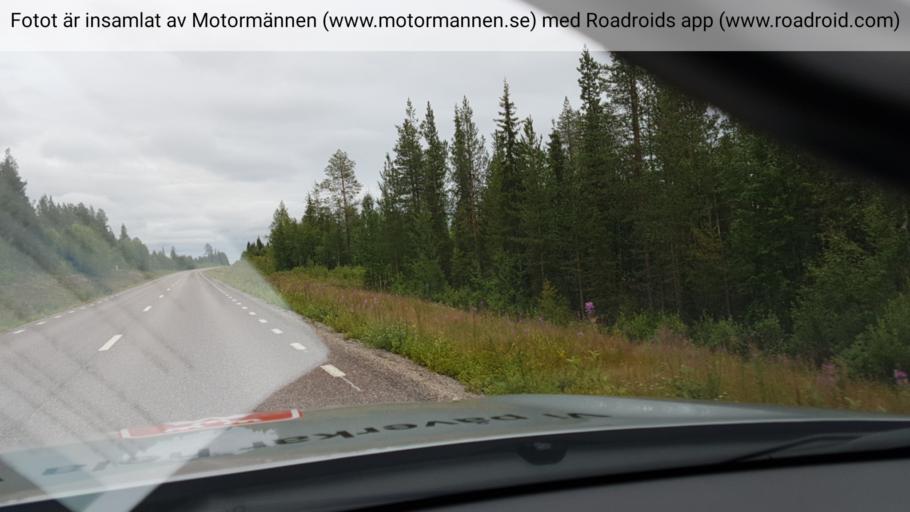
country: SE
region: Norrbotten
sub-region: Gallivare Kommun
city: Gaellivare
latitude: 67.0761
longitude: 21.4207
